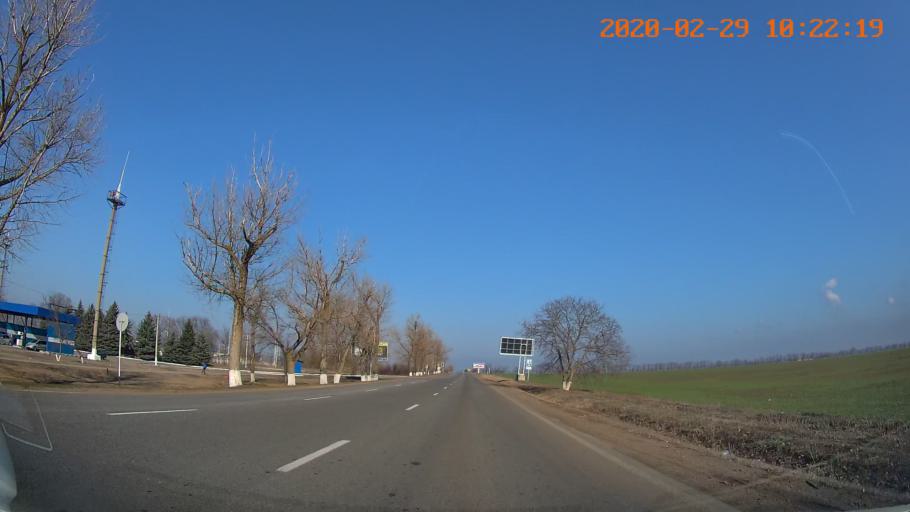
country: MD
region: Telenesti
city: Tiraspolul Nou
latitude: 46.8746
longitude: 29.6072
